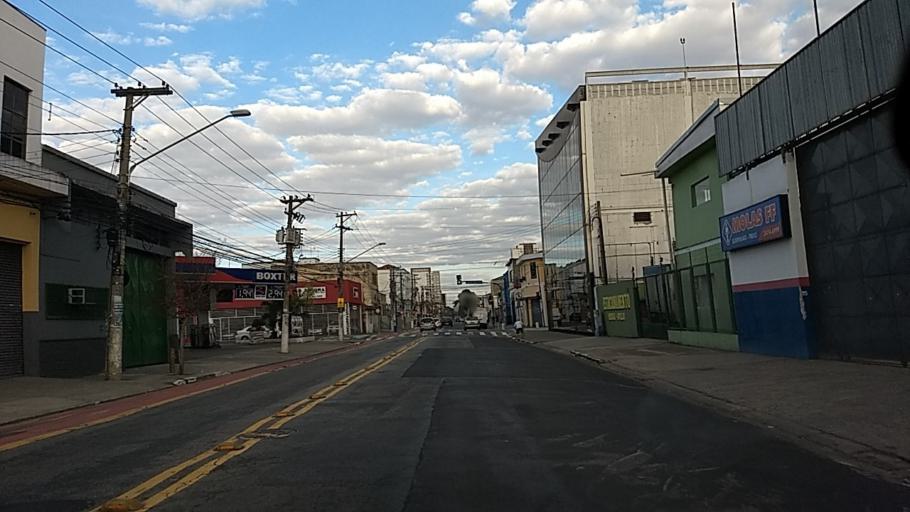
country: BR
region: Sao Paulo
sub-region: Sao Paulo
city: Sao Paulo
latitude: -23.5105
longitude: -46.5942
